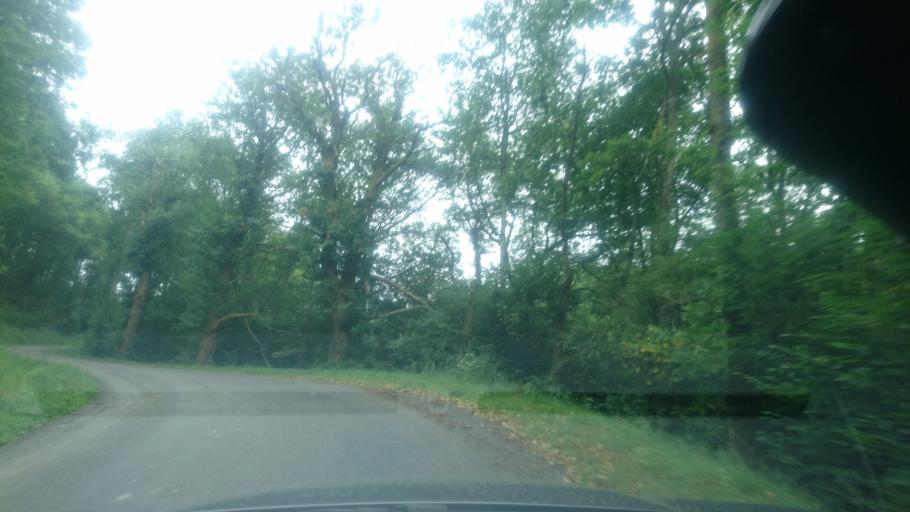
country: FR
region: Midi-Pyrenees
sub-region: Departement des Hautes-Pyrenees
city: Odos
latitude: 43.1437
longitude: 0.0464
